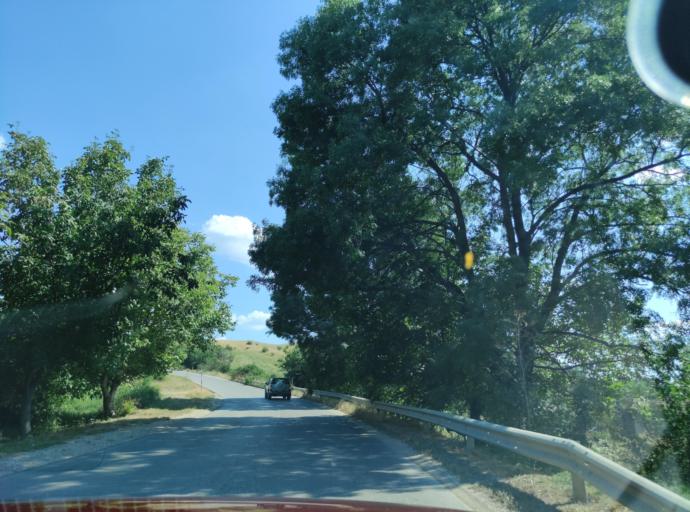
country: BG
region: Pleven
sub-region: Obshtina Cherven Bryag
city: Koynare
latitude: 43.3751
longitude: 24.0587
